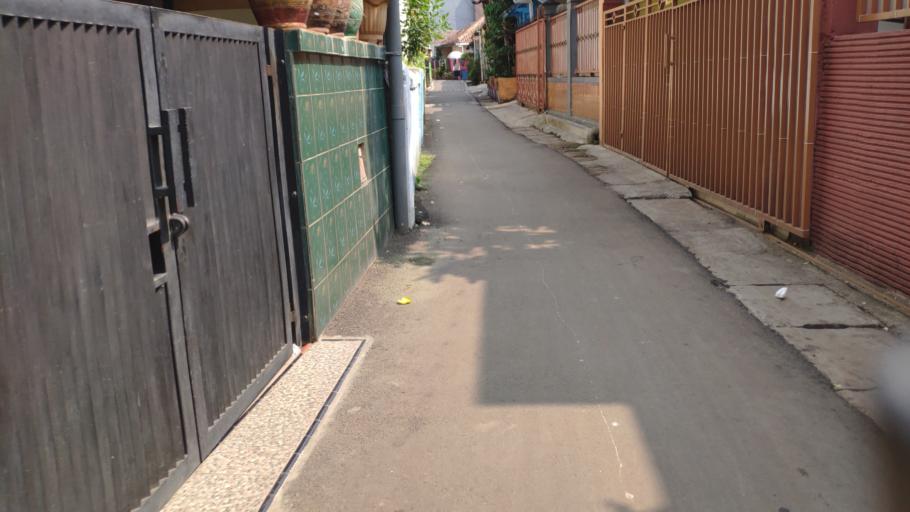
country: ID
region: Jakarta Raya
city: Jakarta
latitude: -6.3035
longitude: 106.8279
